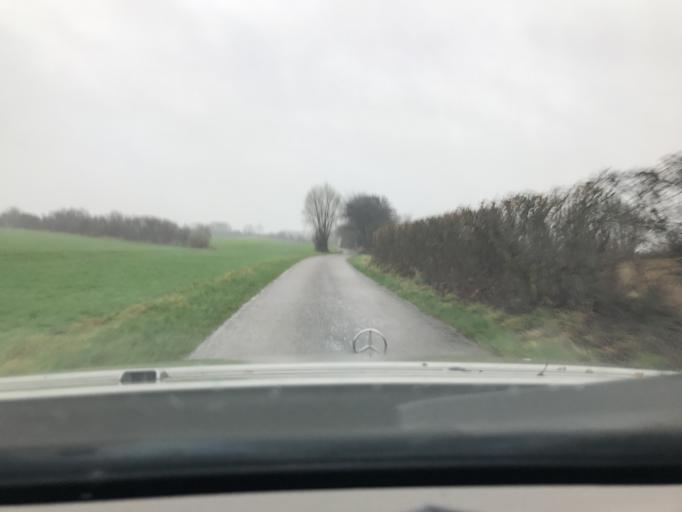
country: DE
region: Schleswig-Holstein
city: Pommerby
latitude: 54.8833
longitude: 10.0621
